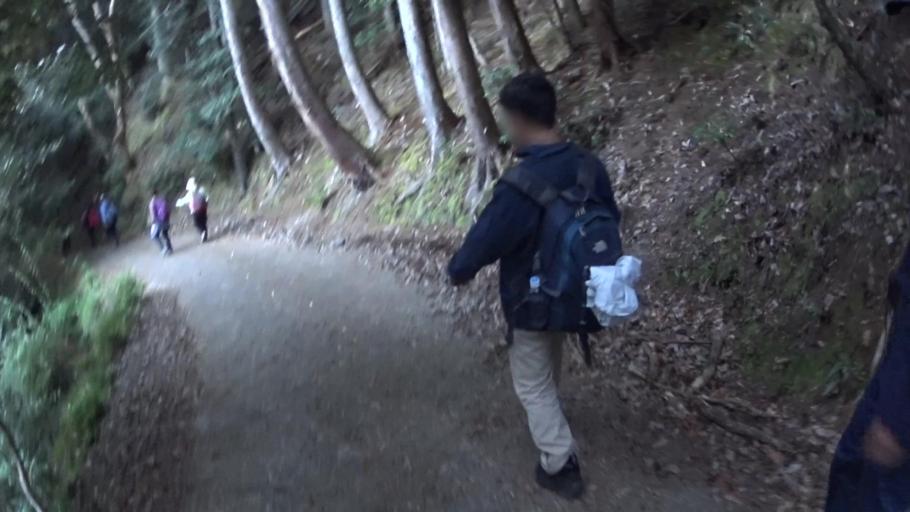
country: JP
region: Kyoto
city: Kameoka
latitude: 35.0457
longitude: 135.6551
